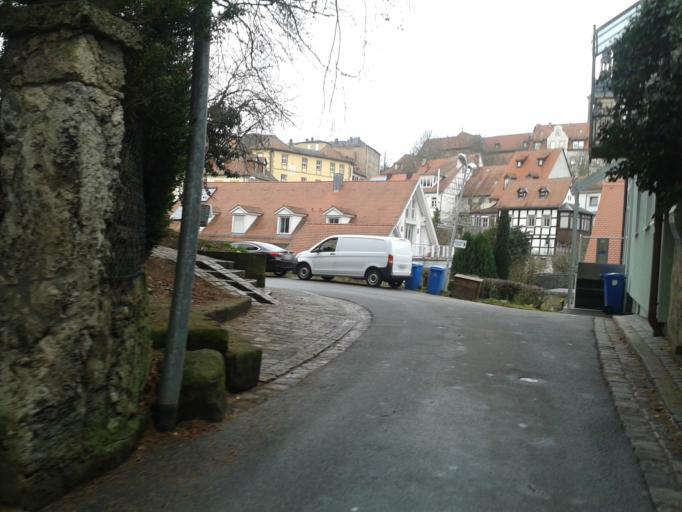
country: DE
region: Bavaria
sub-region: Upper Franconia
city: Bamberg
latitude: 49.8891
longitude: 10.8785
